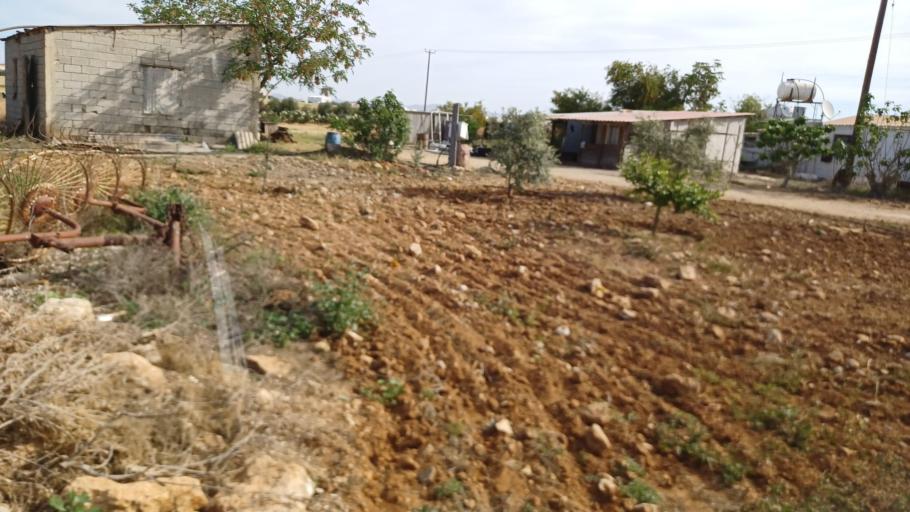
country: CY
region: Lefkosia
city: Kokkinotrimithia
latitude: 35.1631
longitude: 33.1936
